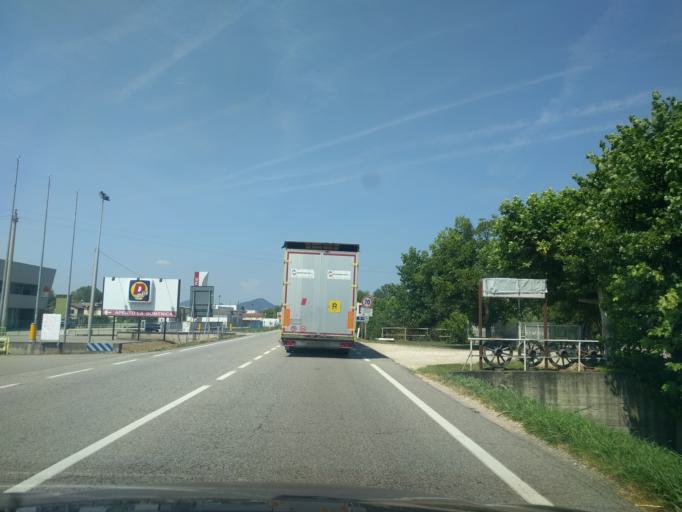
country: IT
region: Veneto
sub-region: Provincia di Padova
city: Solesino
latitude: 45.1839
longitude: 11.7560
